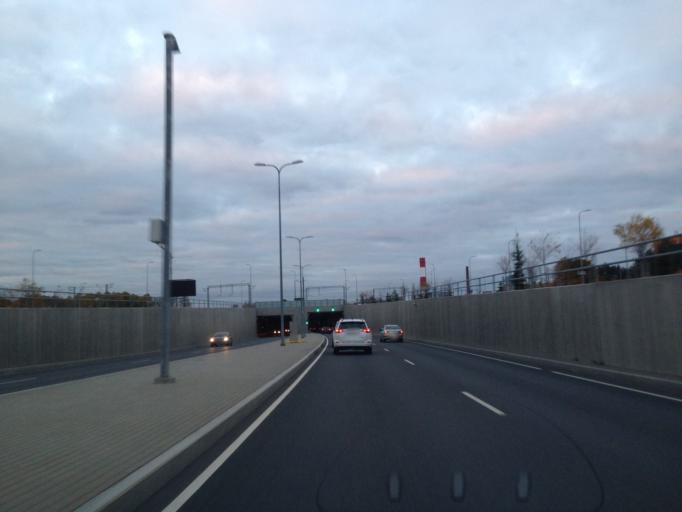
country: EE
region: Harju
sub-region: Tallinna linn
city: Tallinn
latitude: 59.4183
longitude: 24.7659
